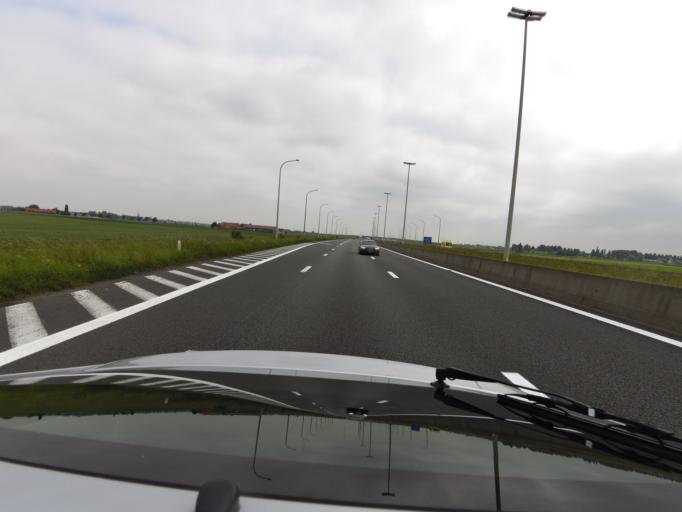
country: BE
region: Flanders
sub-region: Provincie West-Vlaanderen
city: Nieuwpoort
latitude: 51.1072
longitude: 2.7463
